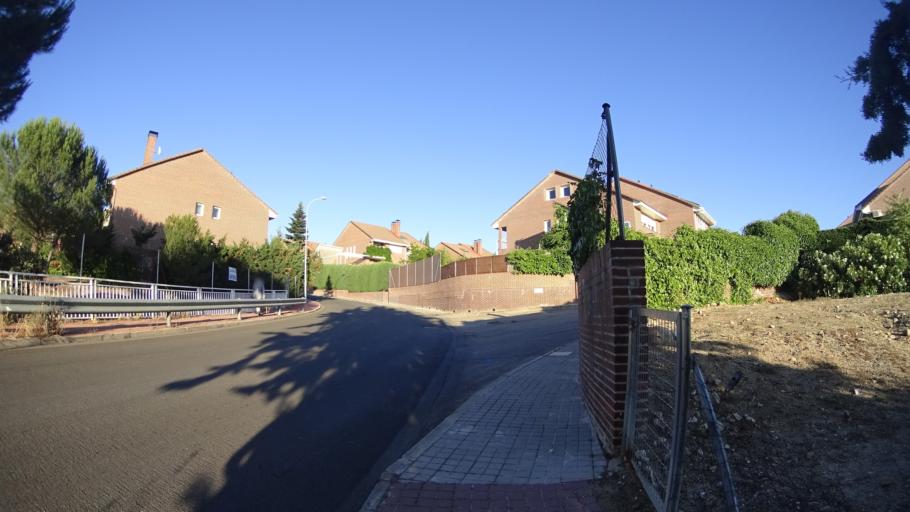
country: ES
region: Madrid
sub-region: Provincia de Madrid
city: Galapagar
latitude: 40.5930
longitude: -3.9711
